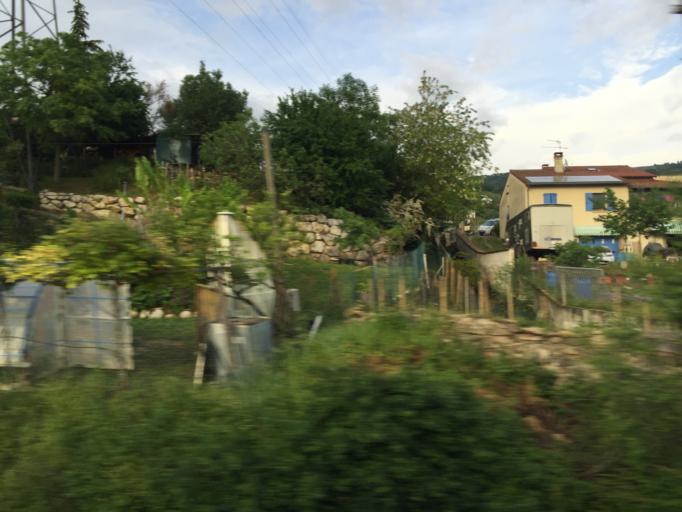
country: FR
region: Rhone-Alpes
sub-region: Departement de l'Ardeche
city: Saint-Jean-de-Muzols
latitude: 45.1104
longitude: 4.8273
